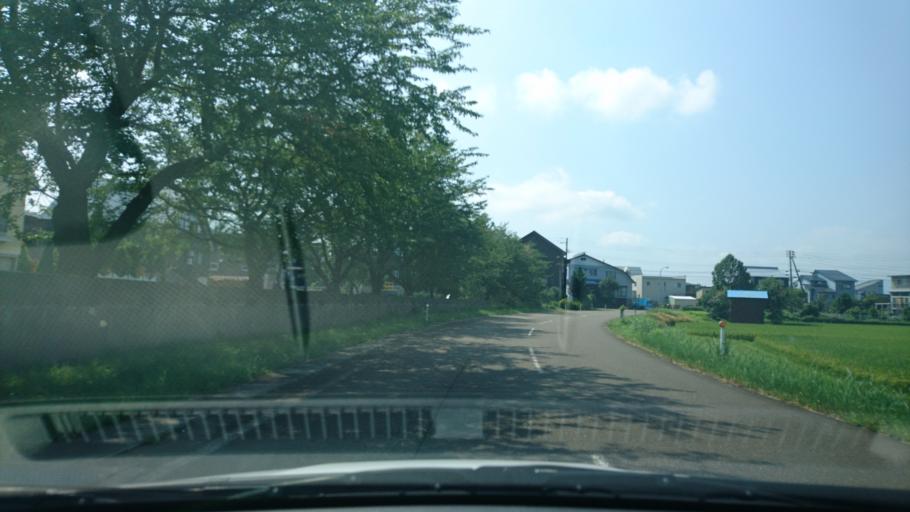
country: JP
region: Niigata
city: Arai
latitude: 37.0597
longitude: 138.2554
